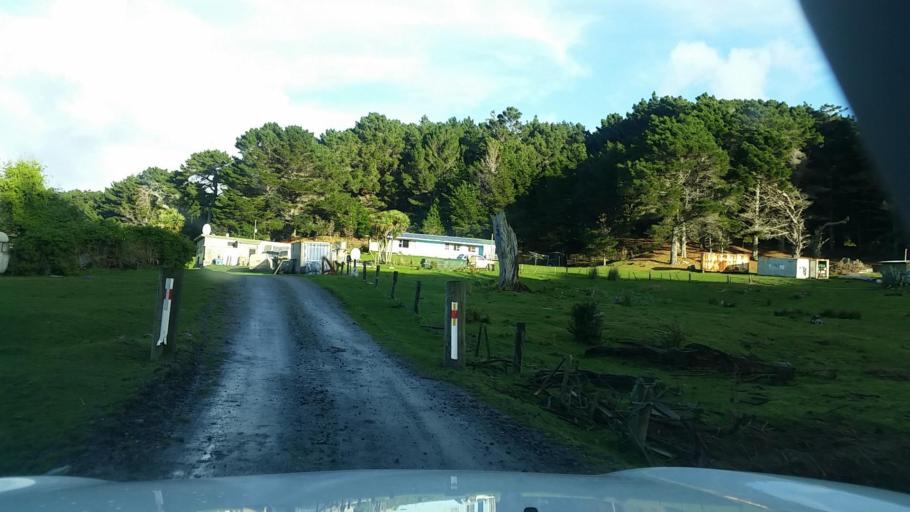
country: NZ
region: Chatham Islands
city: Waitangi
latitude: -43.8141
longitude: -176.7103
